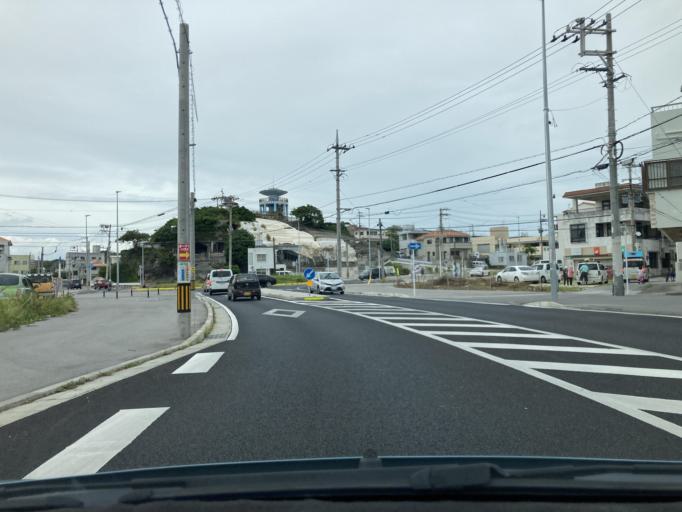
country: JP
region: Okinawa
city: Itoman
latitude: 26.1287
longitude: 127.6696
